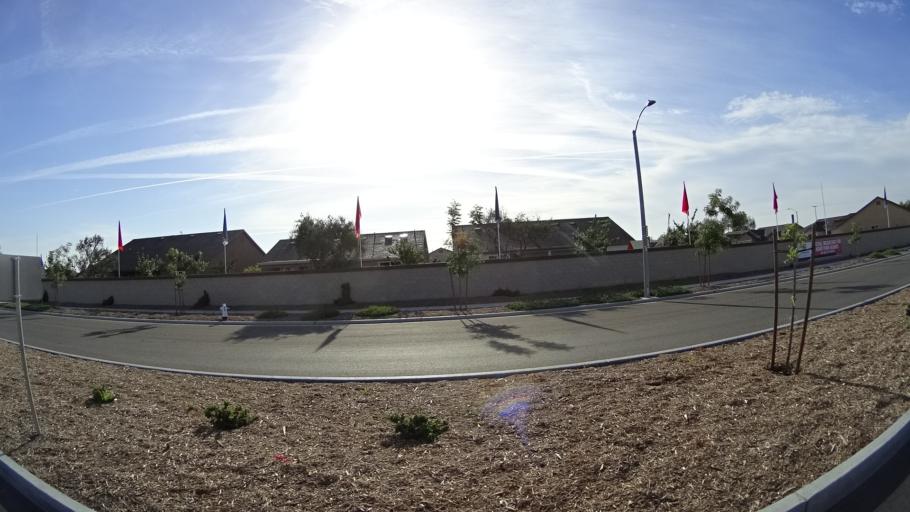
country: US
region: California
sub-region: Kings County
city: Hanford
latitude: 36.3068
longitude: -119.6730
